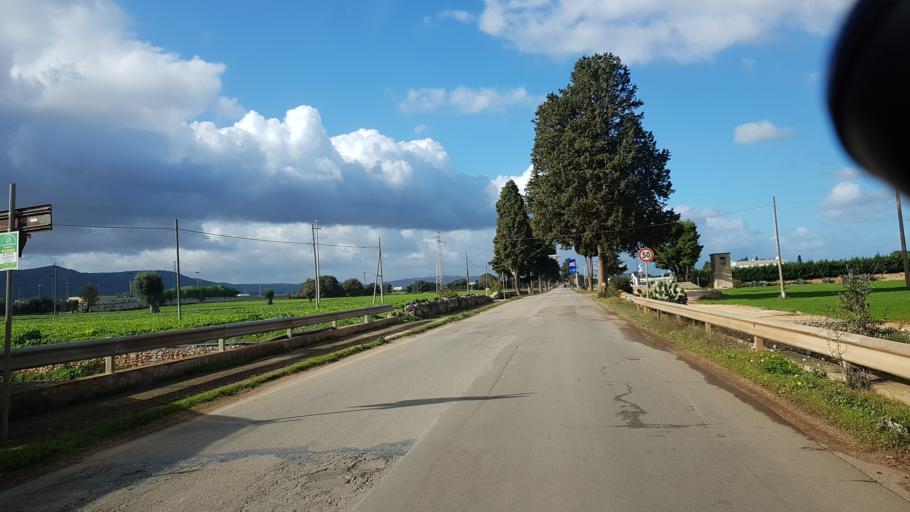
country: IT
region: Apulia
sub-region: Provincia di Brindisi
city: Montalbano
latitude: 40.7835
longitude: 17.4778
